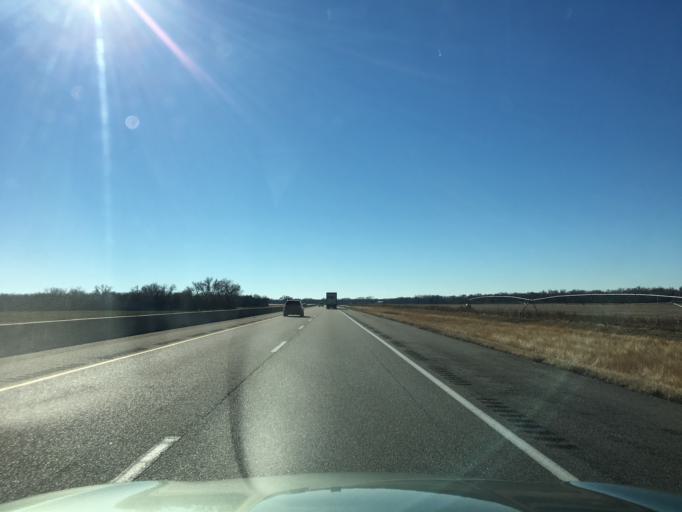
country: US
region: Kansas
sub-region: Sumner County
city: Belle Plaine
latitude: 37.4046
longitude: -97.3244
